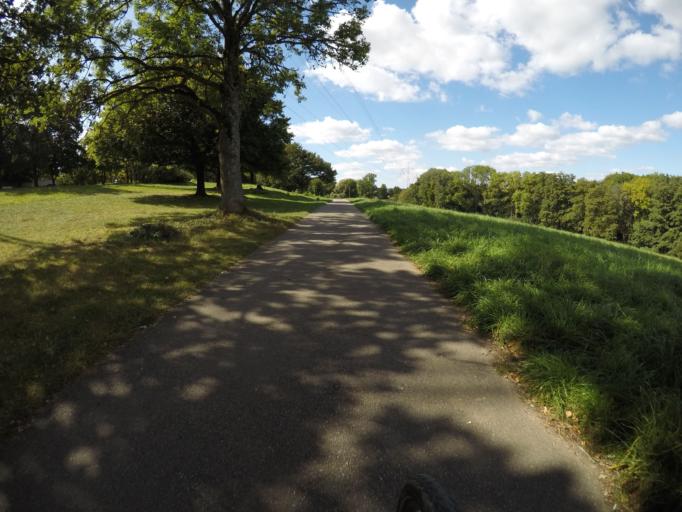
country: DE
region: Baden-Wuerttemberg
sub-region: Regierungsbezirk Stuttgart
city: Leinfelden-Echterdingen
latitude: 48.7161
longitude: 9.1549
